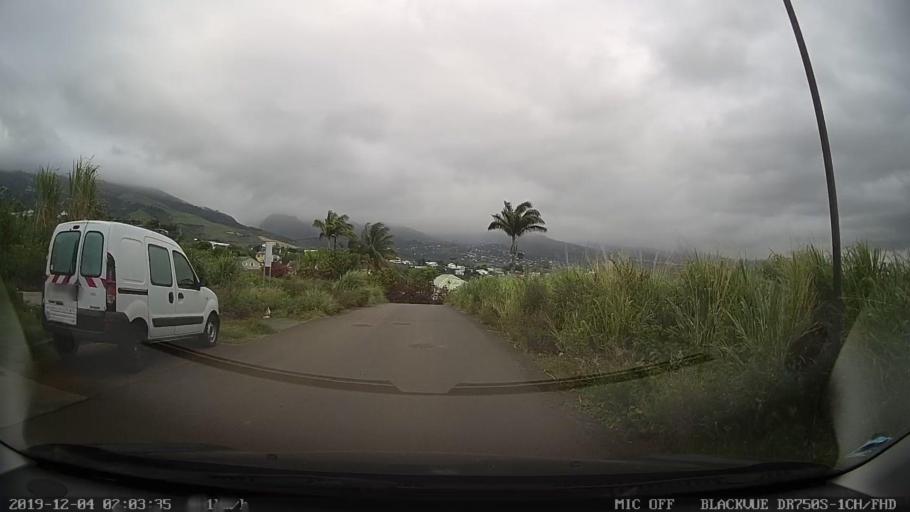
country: RE
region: Reunion
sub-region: Reunion
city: Sainte-Marie
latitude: -20.9214
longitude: 55.5257
